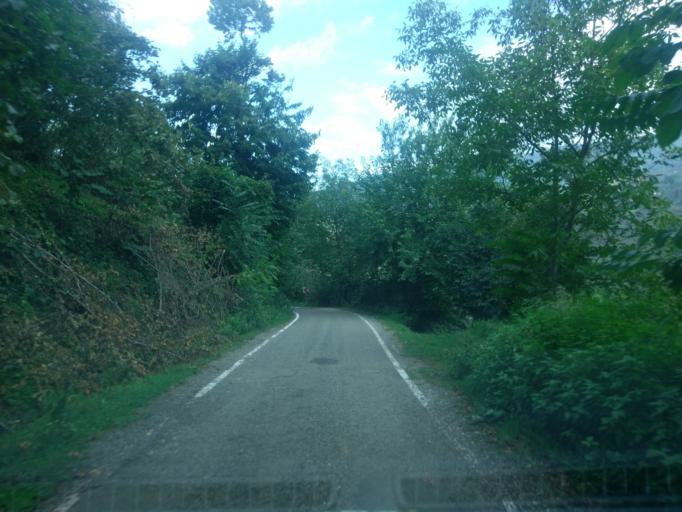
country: TR
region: Ordu
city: Camas
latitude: 40.9370
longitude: 37.6229
